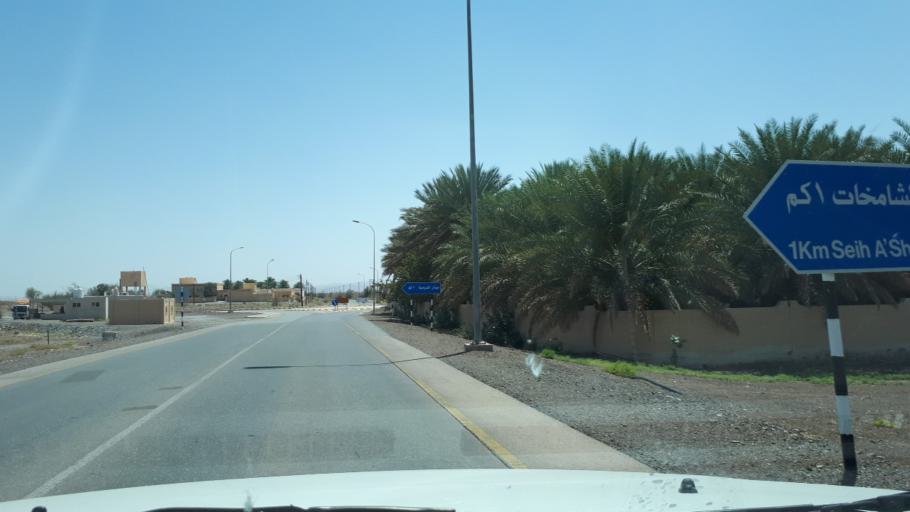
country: OM
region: Muhafazat ad Dakhiliyah
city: Bahla'
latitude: 22.9150
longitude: 57.2527
